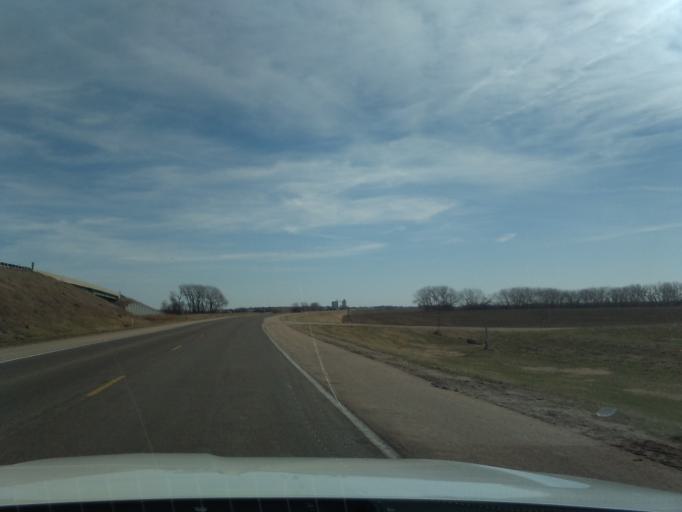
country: US
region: Nebraska
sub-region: Saline County
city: Friend
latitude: 40.6545
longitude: -97.1610
